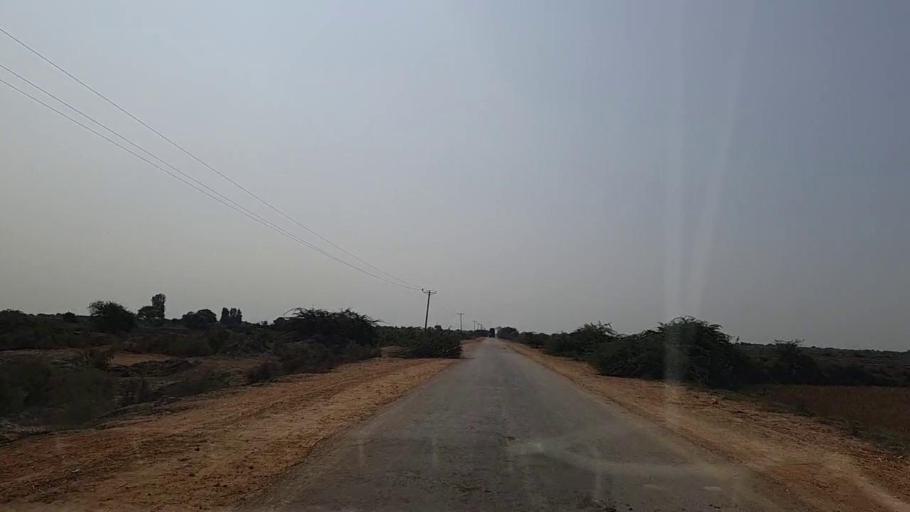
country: PK
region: Sindh
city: Chuhar Jamali
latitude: 24.2817
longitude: 67.9201
